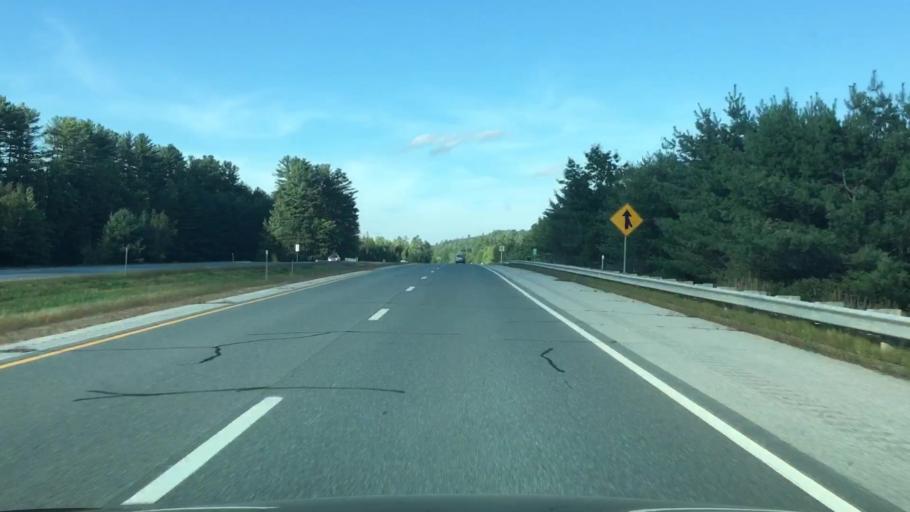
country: US
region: New Hampshire
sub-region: Grafton County
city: Littleton
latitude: 44.2586
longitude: -71.7535
